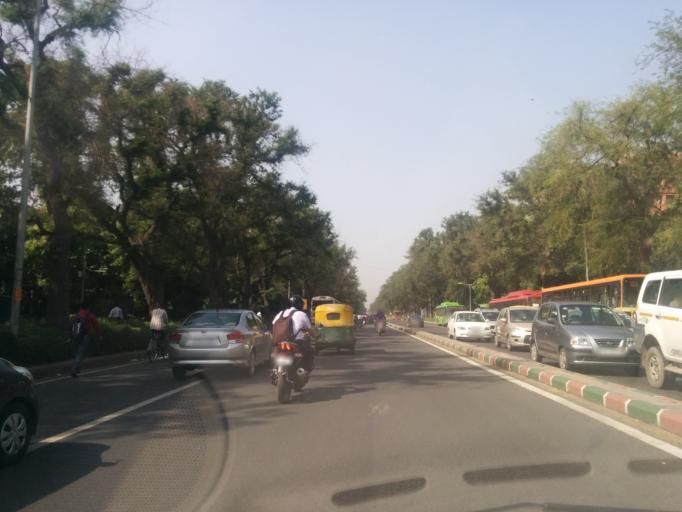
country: IN
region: NCT
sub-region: New Delhi
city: New Delhi
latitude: 28.6247
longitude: 77.2399
